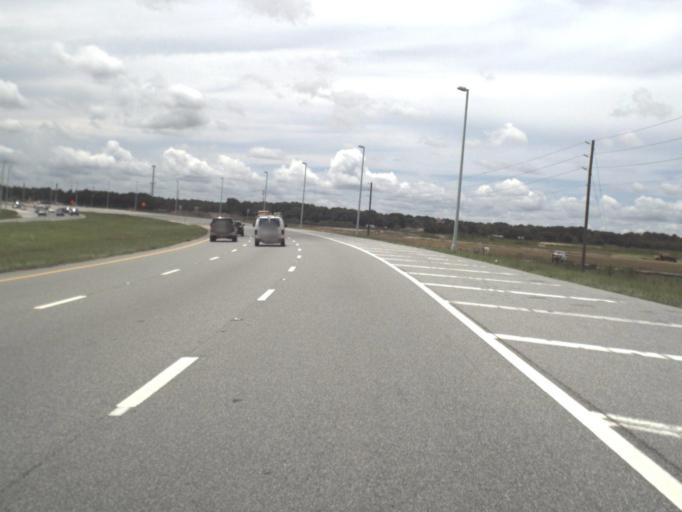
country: US
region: Florida
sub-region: Hillsborough County
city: Pebble Creek
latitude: 28.1951
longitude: -82.3890
